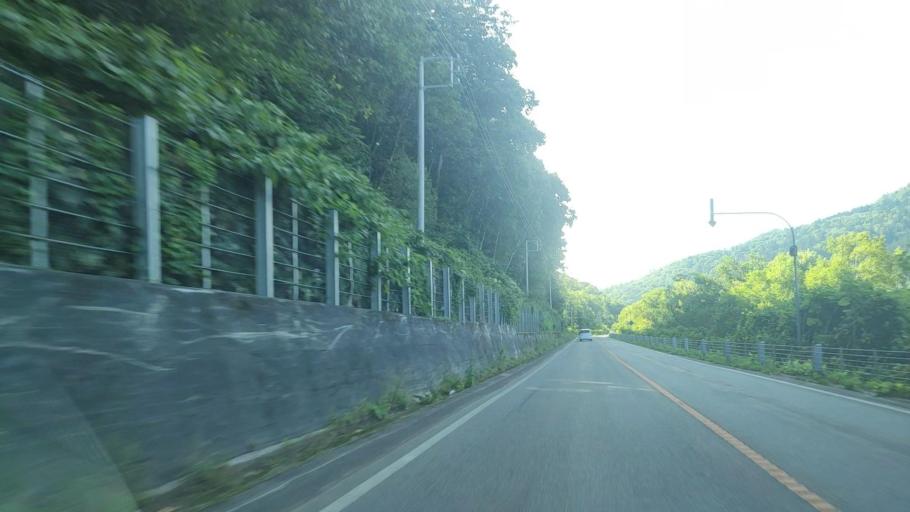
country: JP
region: Hokkaido
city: Nayoro
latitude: 44.7220
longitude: 142.2432
